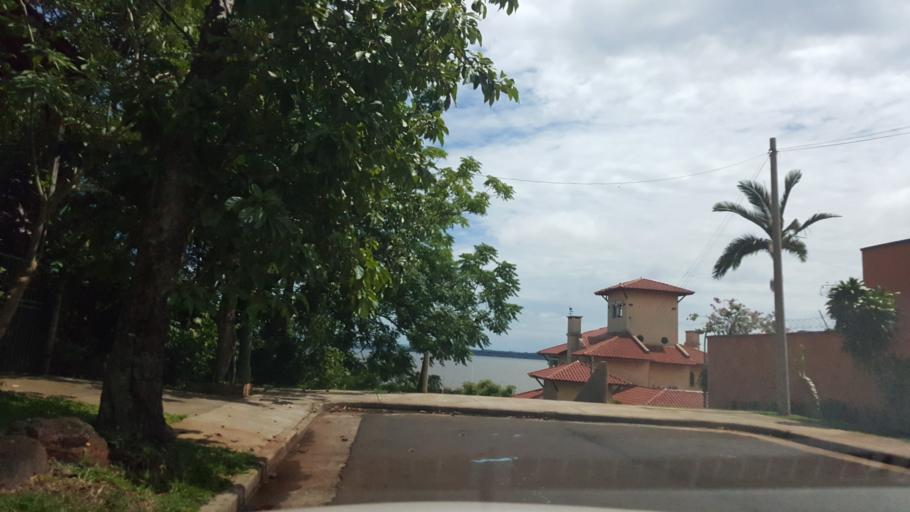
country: AR
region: Misiones
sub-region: Departamento de Capital
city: Posadas
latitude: -27.3554
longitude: -55.9121
